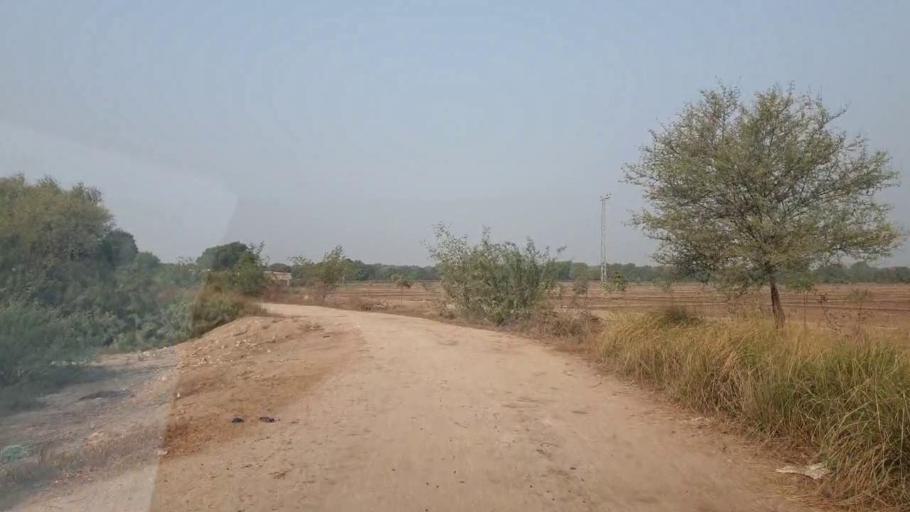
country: PK
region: Sindh
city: Tando Jam
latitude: 25.3305
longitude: 68.5223
